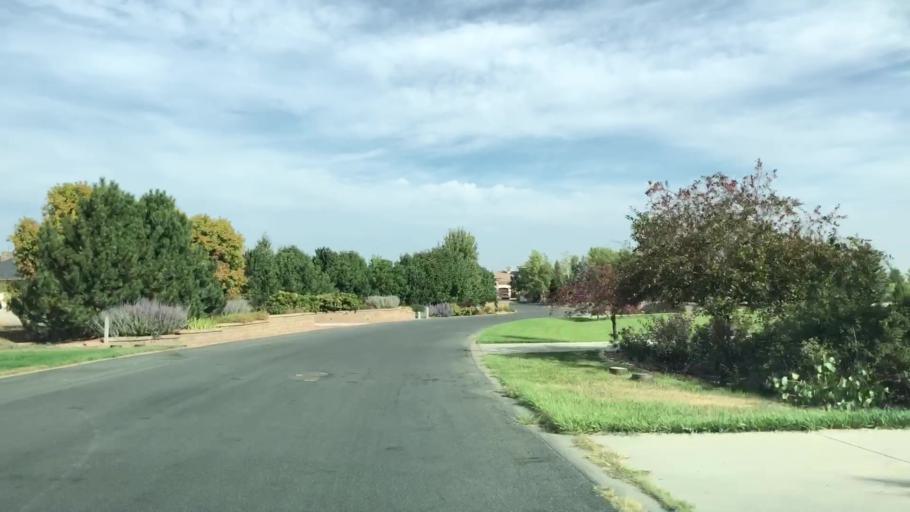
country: US
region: Colorado
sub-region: Larimer County
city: Loveland
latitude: 40.4382
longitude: -105.0548
